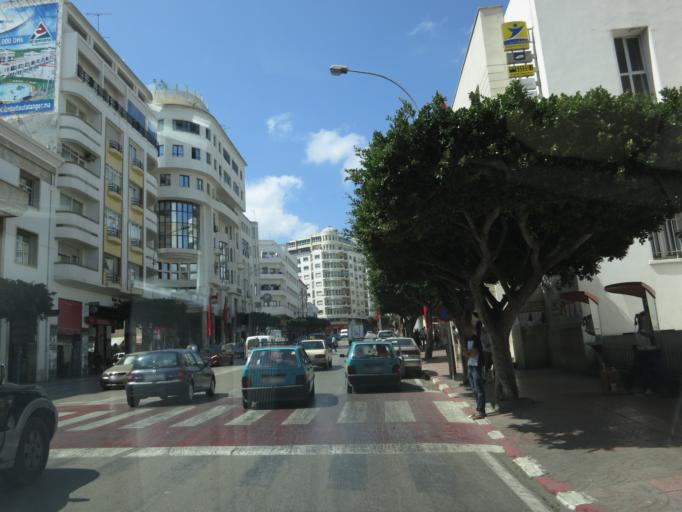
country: MA
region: Tanger-Tetouan
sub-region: Tanger-Assilah
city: Tangier
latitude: 35.7780
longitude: -5.8069
